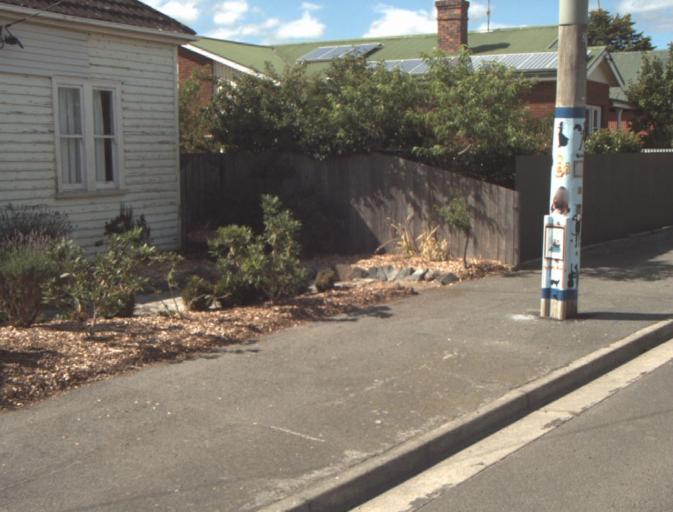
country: AU
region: Tasmania
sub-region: Launceston
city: Mayfield
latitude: -41.2521
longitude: 147.2164
